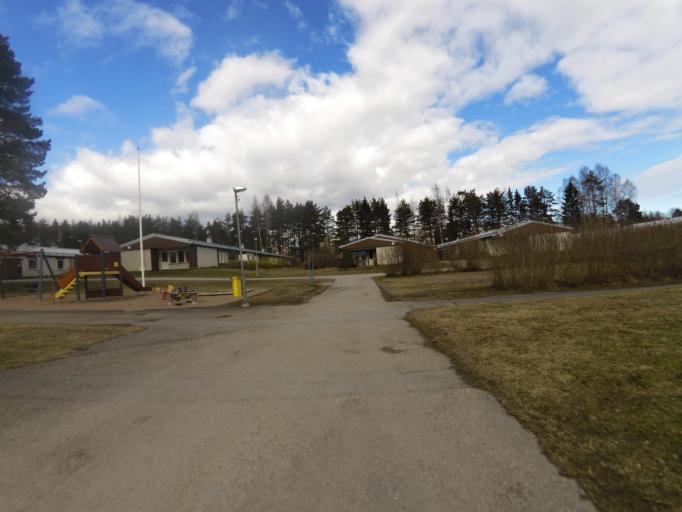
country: SE
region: Gaevleborg
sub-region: Gavle Kommun
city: Gavle
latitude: 60.6883
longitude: 17.1109
